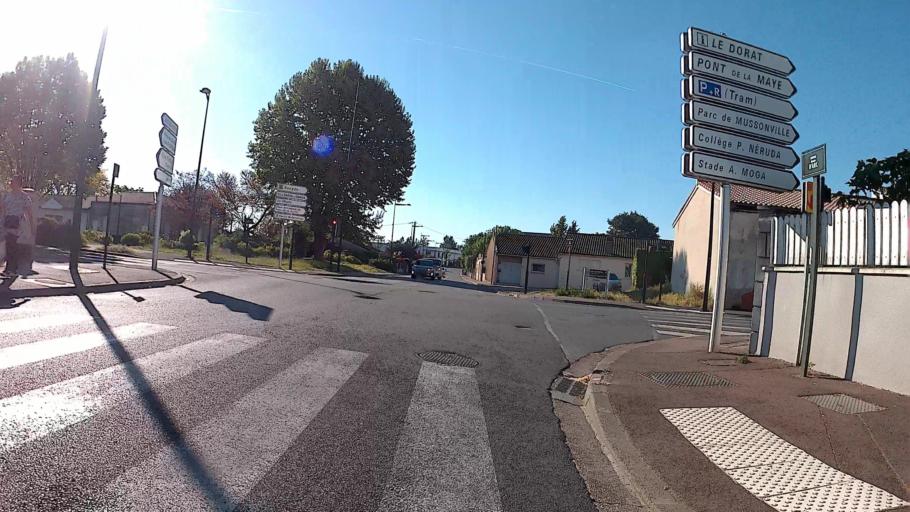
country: FR
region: Aquitaine
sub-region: Departement de la Gironde
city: Begles
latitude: 44.8002
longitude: -0.5435
